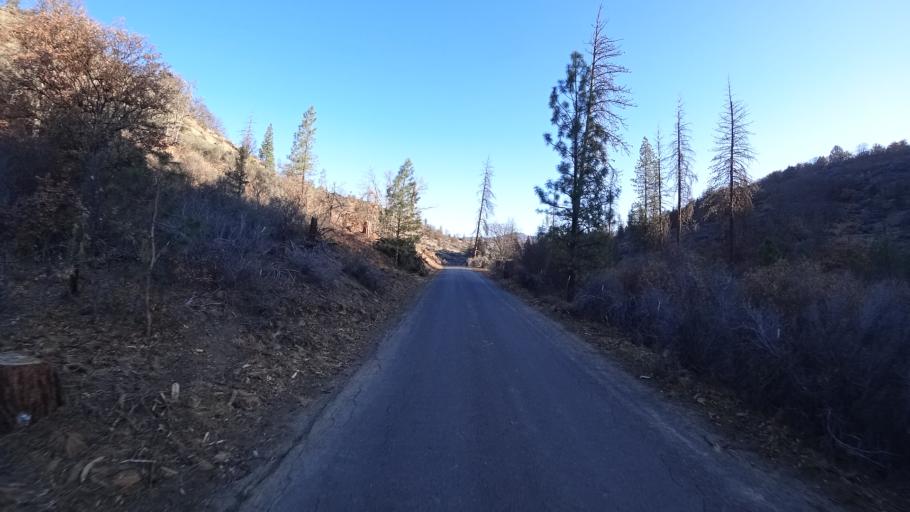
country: US
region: Oregon
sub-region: Jackson County
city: Ashland
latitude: 41.9788
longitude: -122.6275
